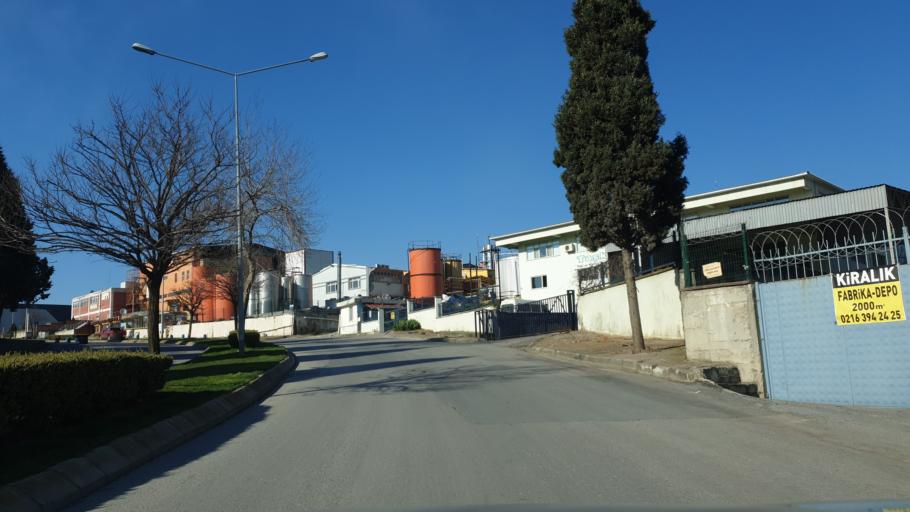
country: TR
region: Kocaeli
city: Balcik
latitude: 40.8794
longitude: 29.3719
